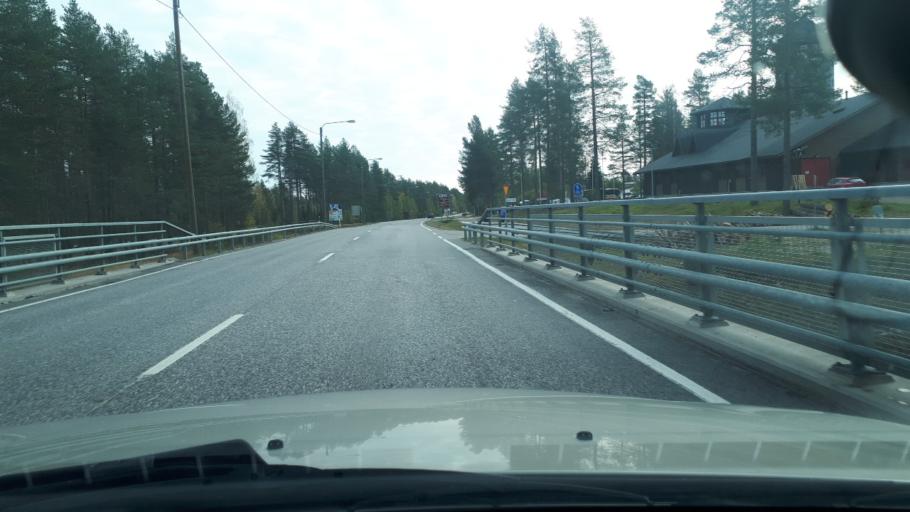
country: FI
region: Lapland
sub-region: Rovaniemi
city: Ranua
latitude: 65.9447
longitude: 26.4654
